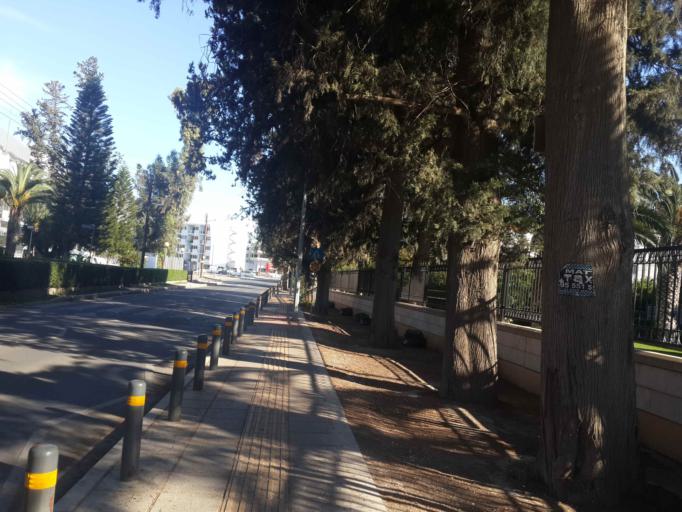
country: CY
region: Lefkosia
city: Nicosia
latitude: 35.1575
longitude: 33.3380
